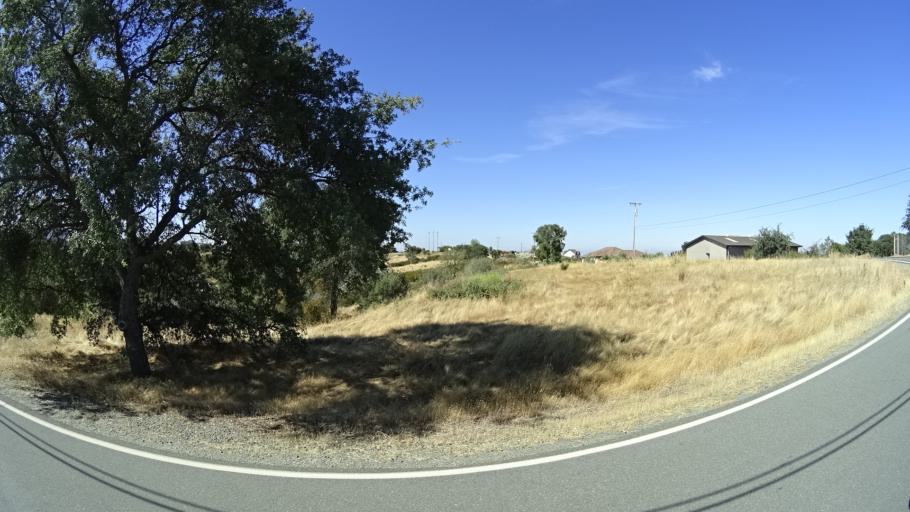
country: US
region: California
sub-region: Calaveras County
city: Valley Springs
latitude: 38.1683
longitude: -120.8606
